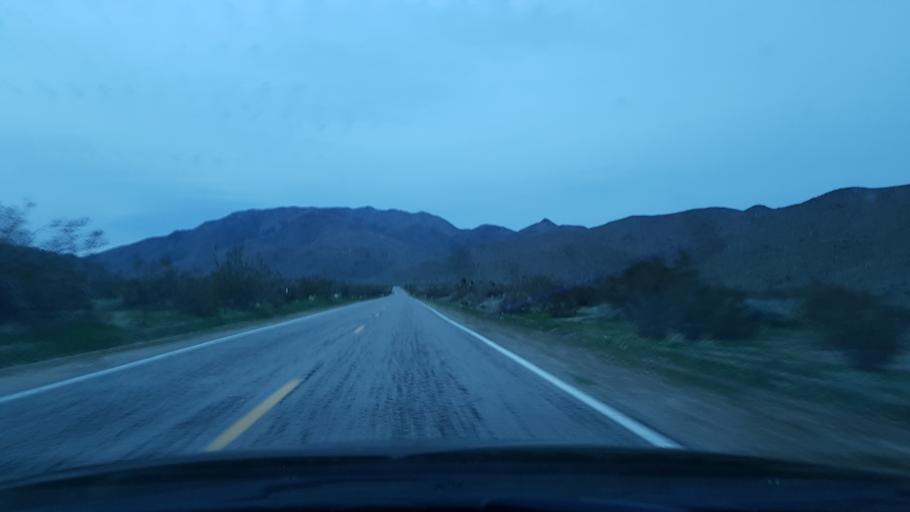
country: US
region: California
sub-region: San Diego County
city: Julian
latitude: 32.9871
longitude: -116.4432
